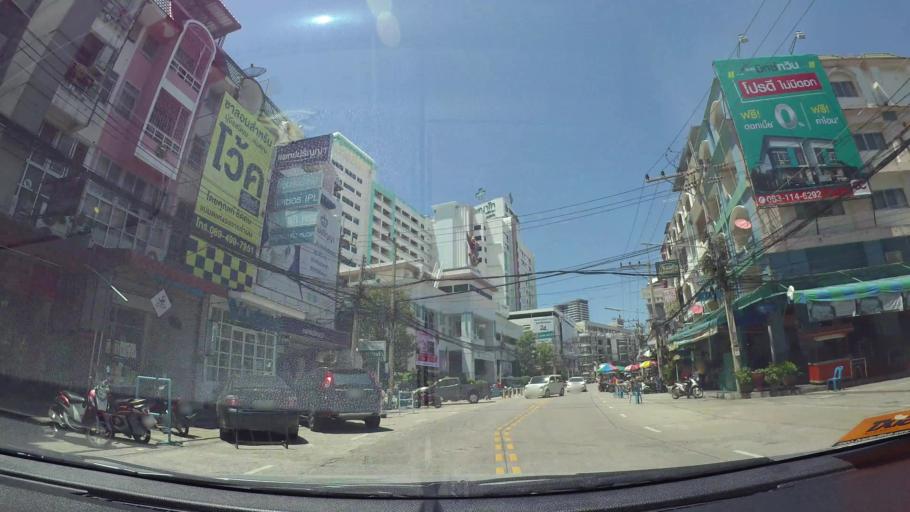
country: TH
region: Chon Buri
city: Si Racha
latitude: 13.1685
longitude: 100.9278
